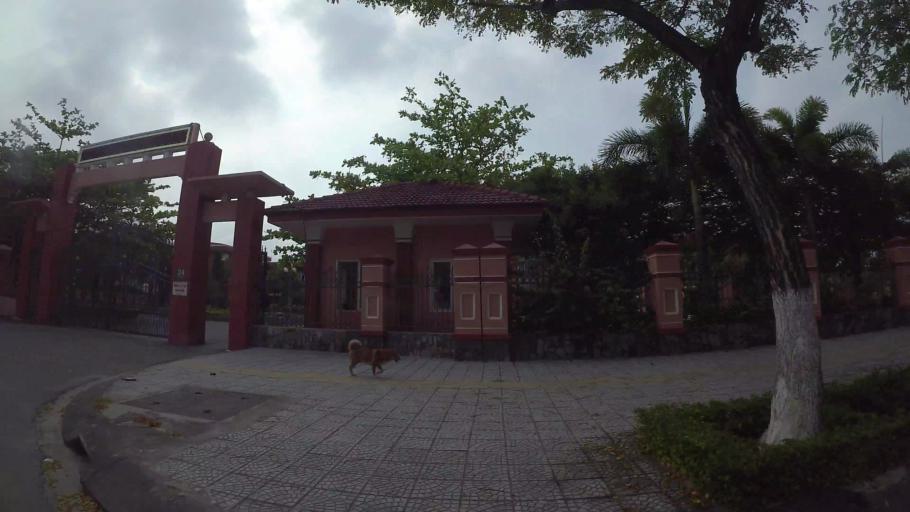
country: VN
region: Da Nang
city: Son Tra
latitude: 16.0787
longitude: 108.2428
